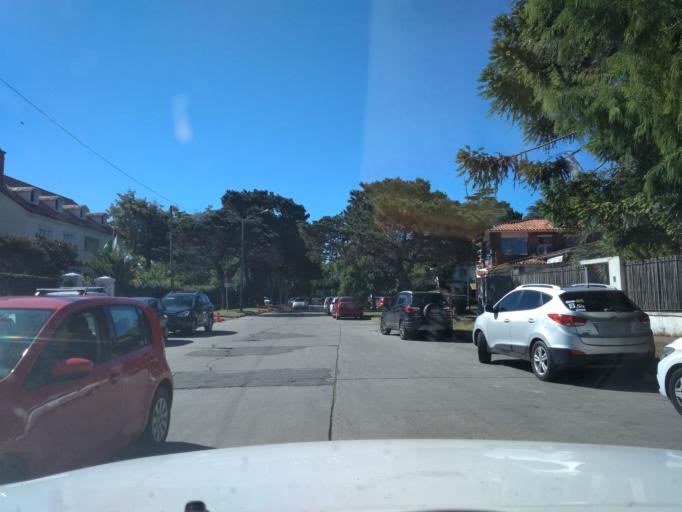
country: UY
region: Canelones
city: Paso de Carrasco
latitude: -34.8881
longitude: -56.0590
